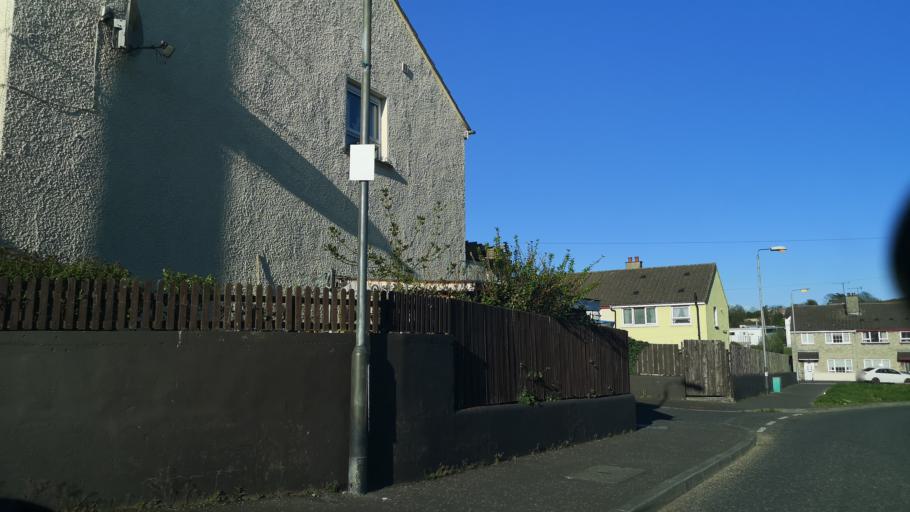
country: GB
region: Northern Ireland
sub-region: Newry and Mourne District
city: Newry
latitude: 54.1821
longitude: -6.3386
